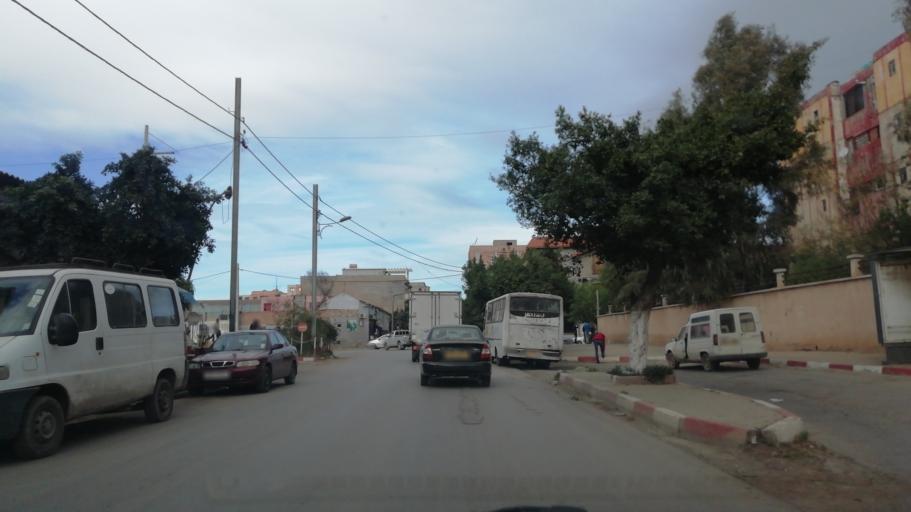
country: DZ
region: Oran
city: Oran
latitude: 35.6840
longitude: -0.6142
